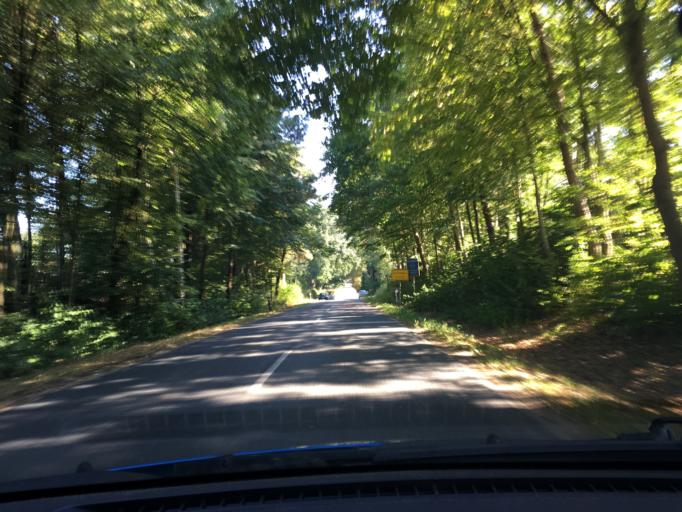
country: DE
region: Lower Saxony
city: Thomasburg
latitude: 53.2282
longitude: 10.7035
